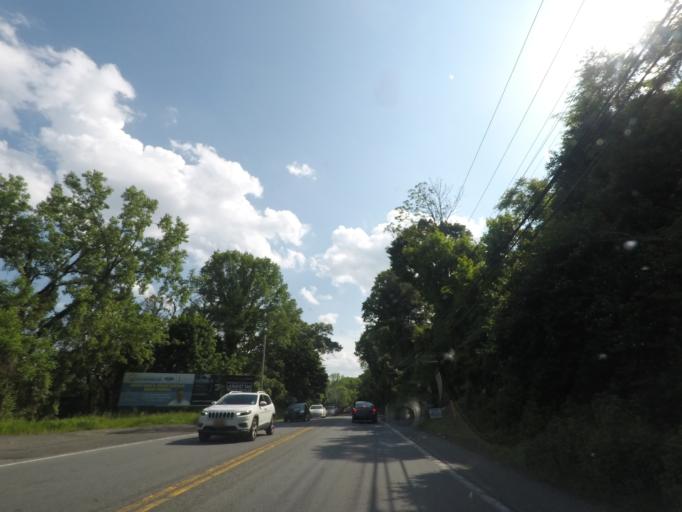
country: US
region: New York
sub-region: Orange County
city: Balmville
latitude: 41.5297
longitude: -74.0177
